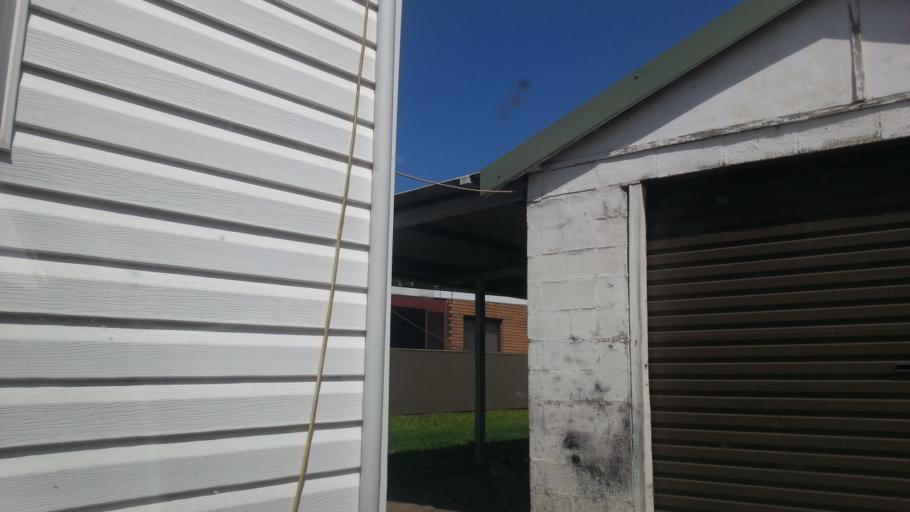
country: AU
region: New South Wales
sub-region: Wollongong
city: Gwynneville
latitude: -34.4124
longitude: 150.8863
